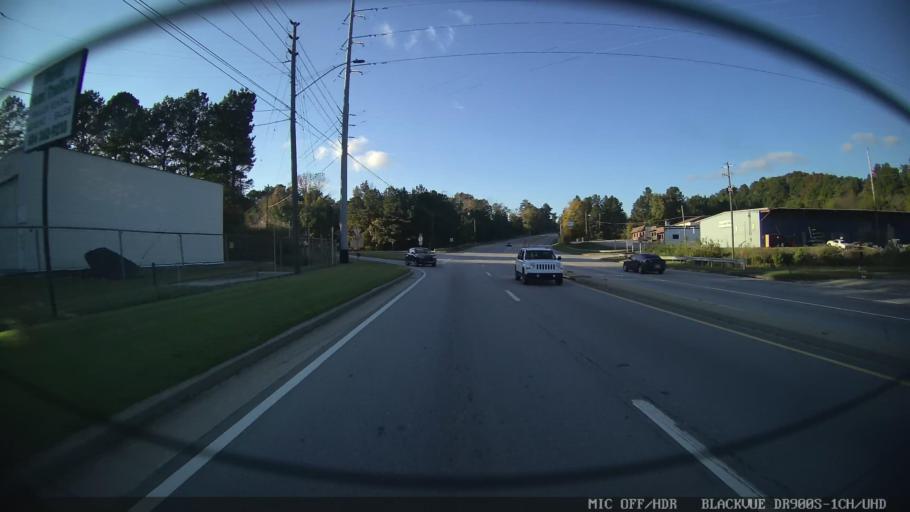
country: US
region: Georgia
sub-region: Clayton County
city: Conley
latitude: 33.6481
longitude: -84.3301
